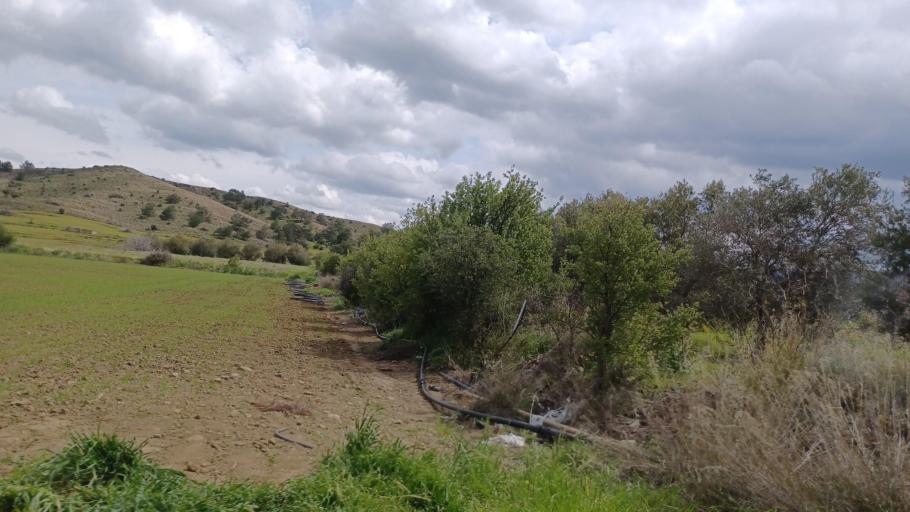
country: CY
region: Lefkosia
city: Lefka
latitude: 35.0746
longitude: 32.9259
